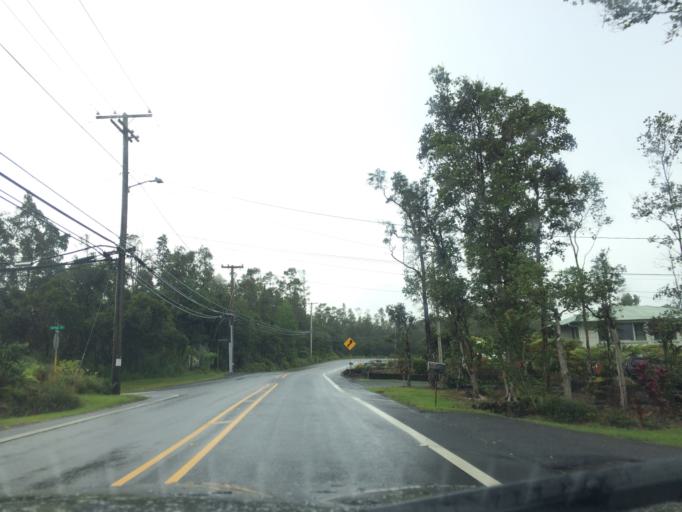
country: US
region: Hawaii
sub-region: Hawaii County
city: Hilo
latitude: 19.6918
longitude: -155.1241
